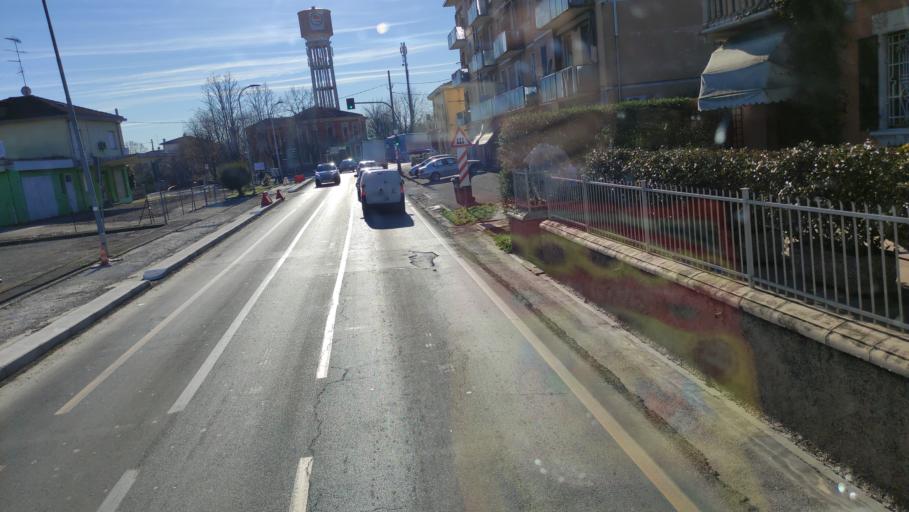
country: IT
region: Emilia-Romagna
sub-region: Provincia di Reggio Emilia
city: Novellara
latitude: 44.8463
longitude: 10.7244
